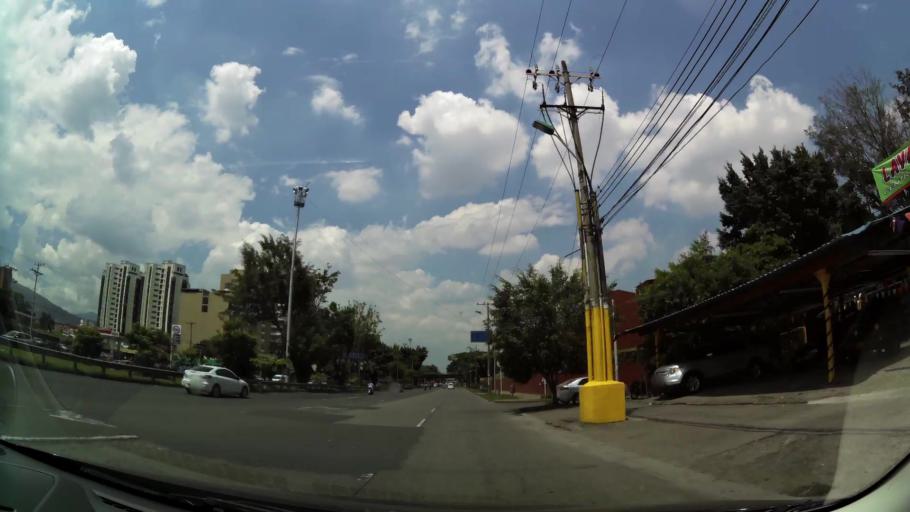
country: CO
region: Valle del Cauca
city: Cali
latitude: 3.4082
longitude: -76.5392
